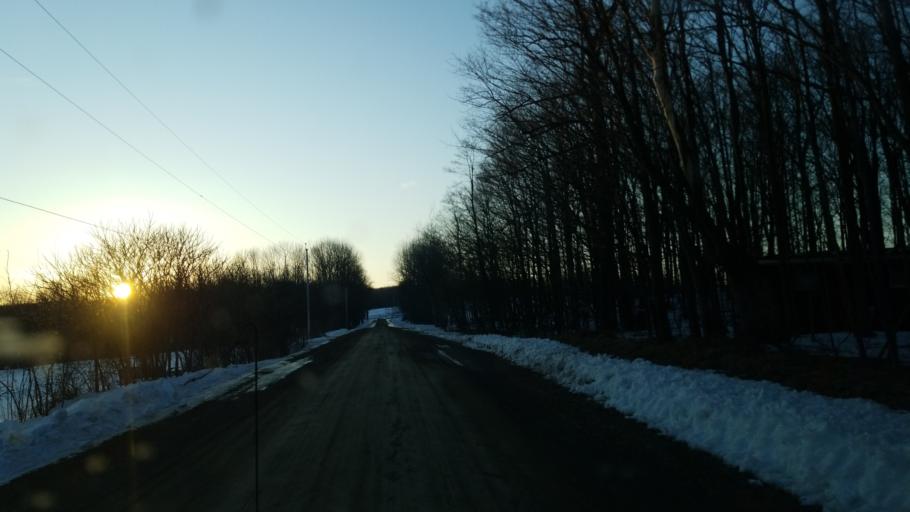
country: US
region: Pennsylvania
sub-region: Tioga County
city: Westfield
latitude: 42.0394
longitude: -77.6152
